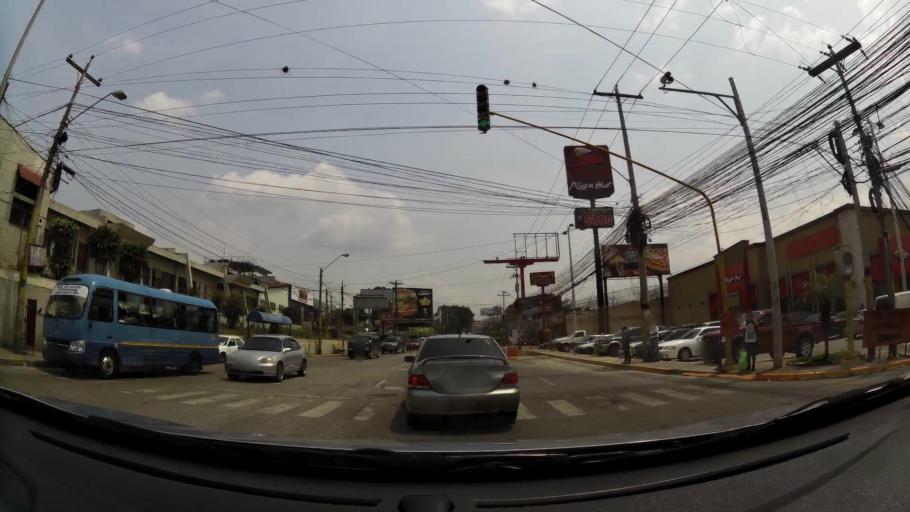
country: HN
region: Francisco Morazan
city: Tegucigalpa
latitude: 14.0596
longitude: -87.2202
